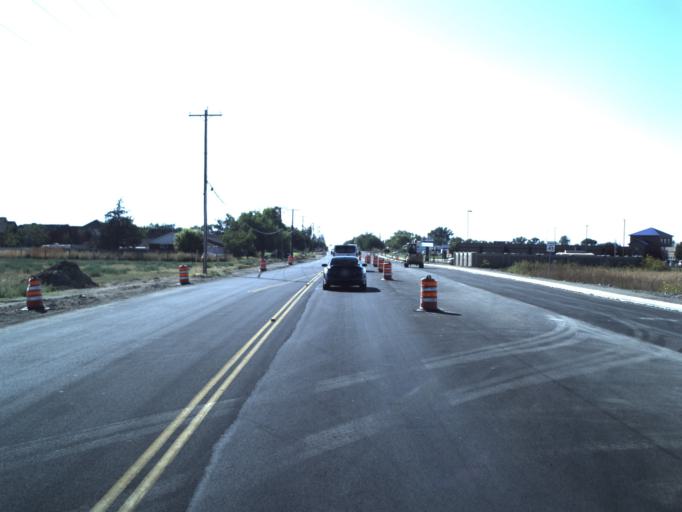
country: US
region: Utah
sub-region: Weber County
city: Hooper
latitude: 41.1908
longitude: -112.0939
